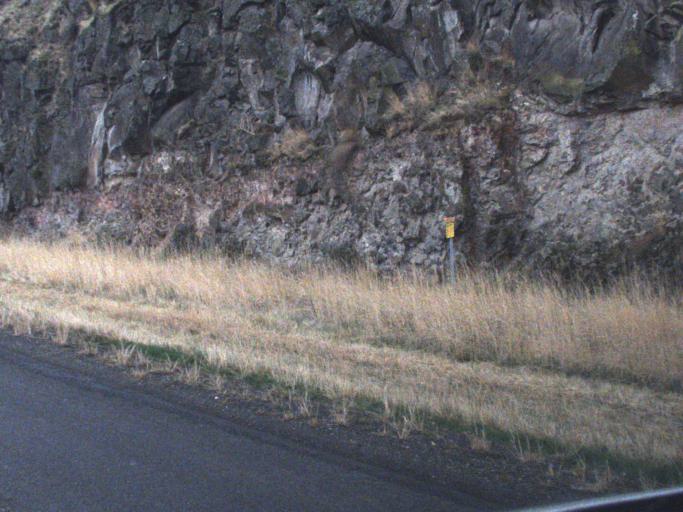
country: US
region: Washington
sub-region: Asotin County
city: Clarkston Heights-Vineland
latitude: 46.4183
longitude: -117.1075
